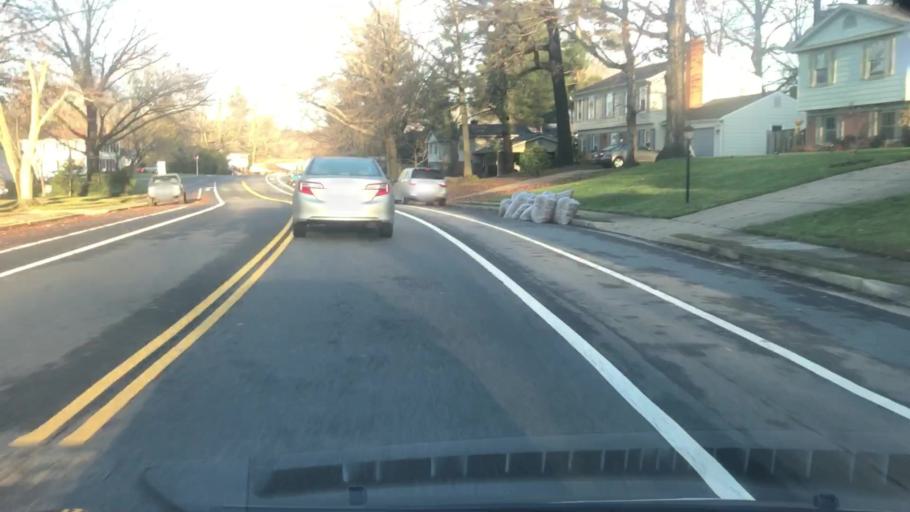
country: US
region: Virginia
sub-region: Fairfax County
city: Kings Park
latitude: 38.8202
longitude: -77.2372
